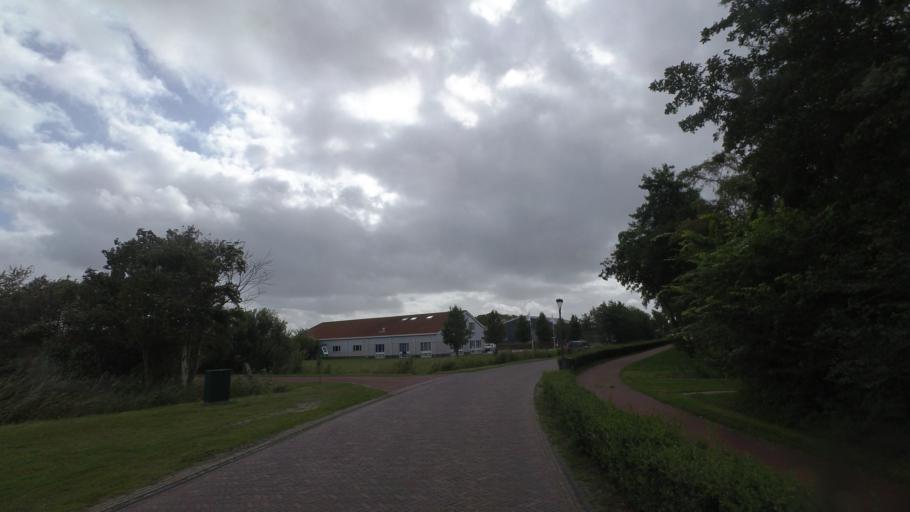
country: NL
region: Friesland
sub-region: Gemeente Ameland
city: Hollum
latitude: 53.4457
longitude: 5.6408
